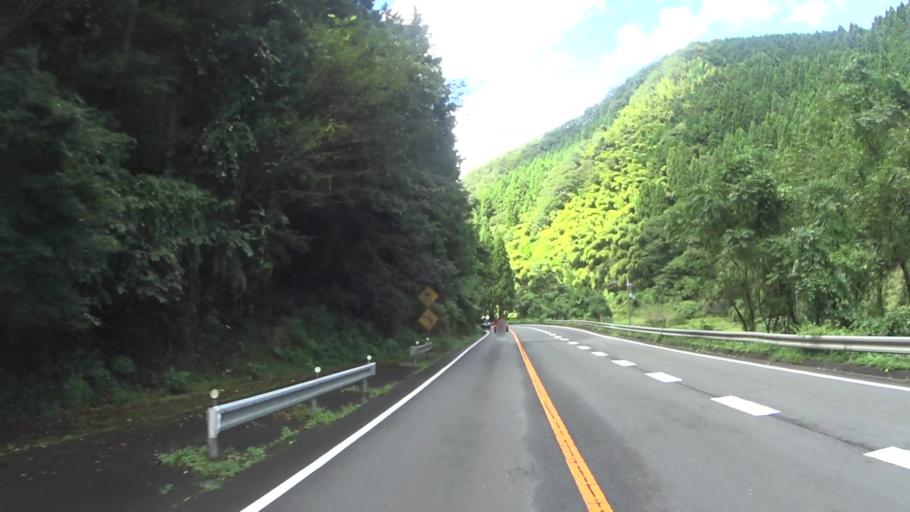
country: JP
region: Kyoto
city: Ayabe
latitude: 35.2441
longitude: 135.3097
